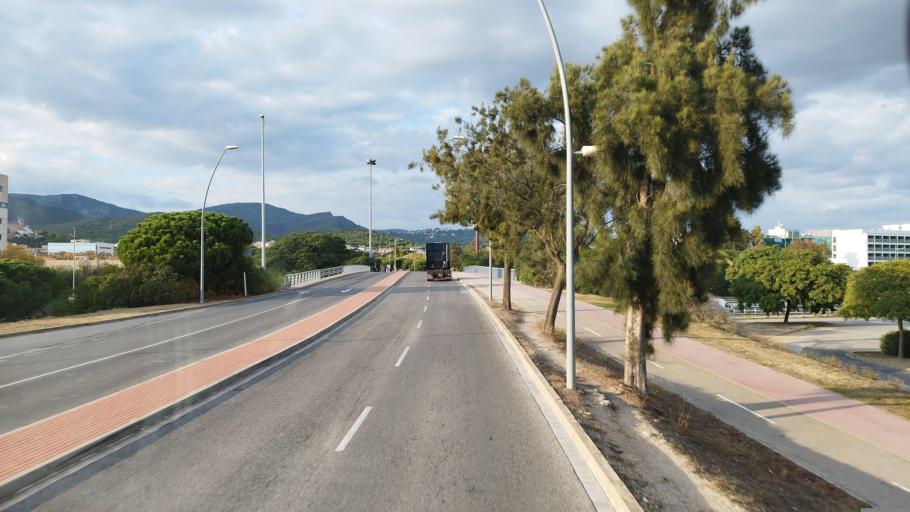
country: ES
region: Catalonia
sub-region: Provincia de Barcelona
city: Castelldefels
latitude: 41.2787
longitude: 1.9896
